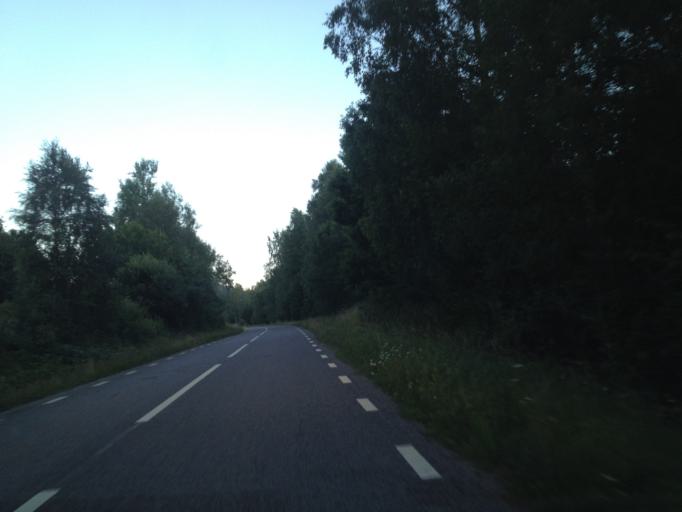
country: SE
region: Kalmar
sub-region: Vasterviks Kommun
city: Overum
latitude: 58.0107
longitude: 16.1728
